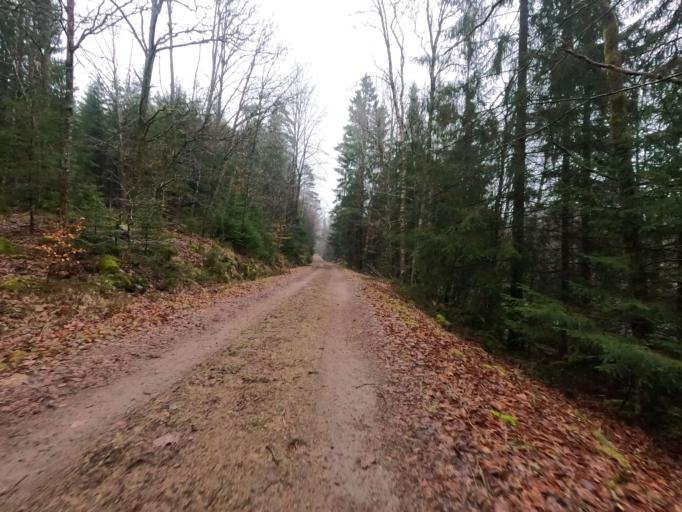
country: SE
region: Halland
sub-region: Hylte Kommun
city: Hyltebruk
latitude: 56.8010
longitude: 13.2235
